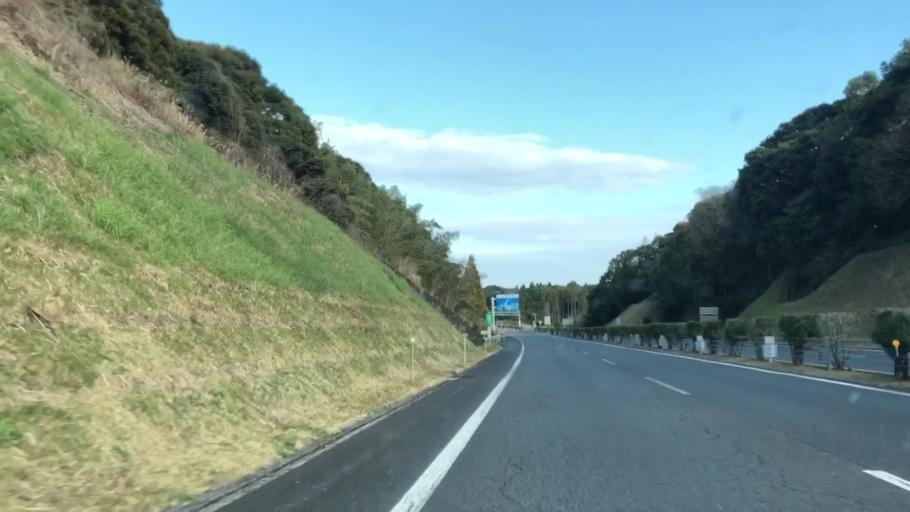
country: JP
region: Miyazaki
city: Miyazaki-shi
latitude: 31.8680
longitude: 131.4069
